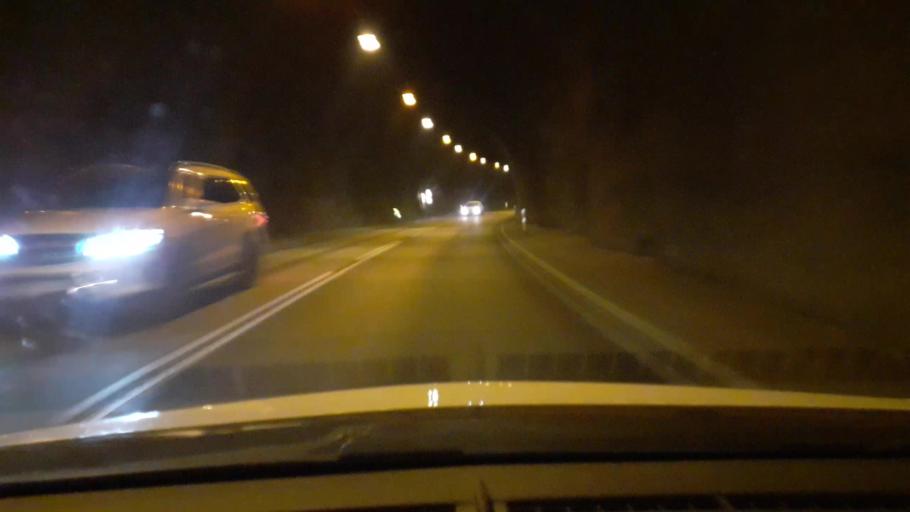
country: IS
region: Capital Region
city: Reykjavik
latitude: 64.2861
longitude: -21.8487
